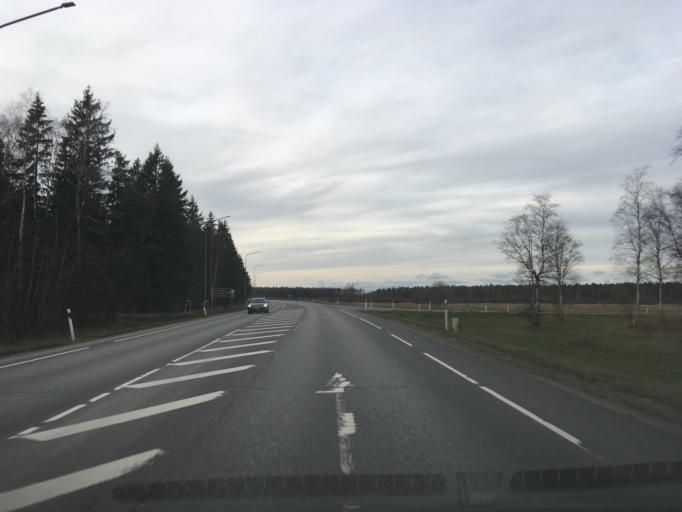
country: EE
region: Ida-Virumaa
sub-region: Kohtla-Jaerve linn
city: Kohtla-Jarve
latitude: 59.4185
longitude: 27.2861
